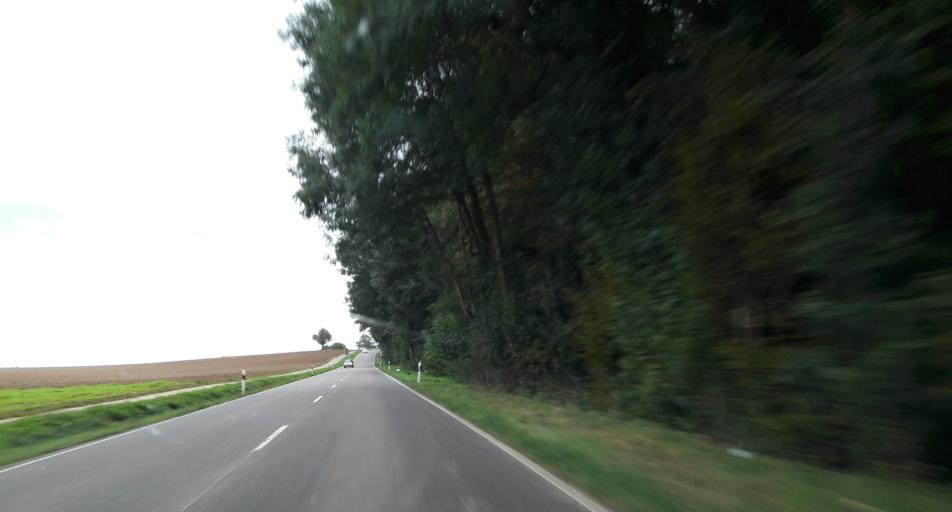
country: DE
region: Baden-Wuerttemberg
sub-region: Regierungsbezirk Stuttgart
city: Kirchardt
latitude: 49.2139
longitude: 8.9790
